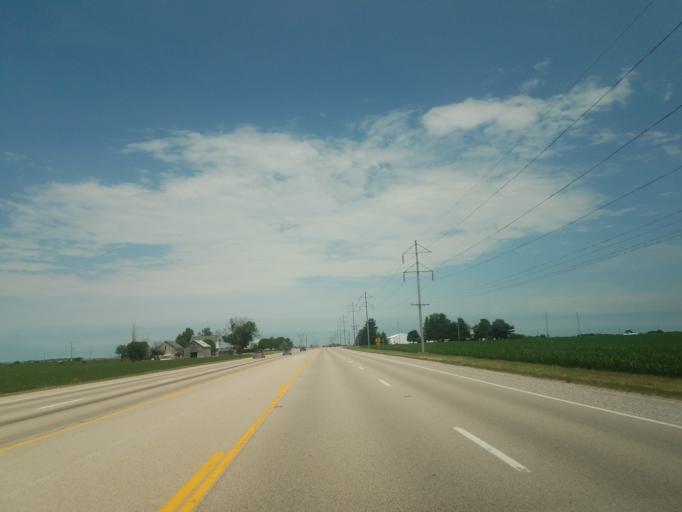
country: US
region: Illinois
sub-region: McLean County
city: Downs
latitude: 40.4408
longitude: -88.9016
